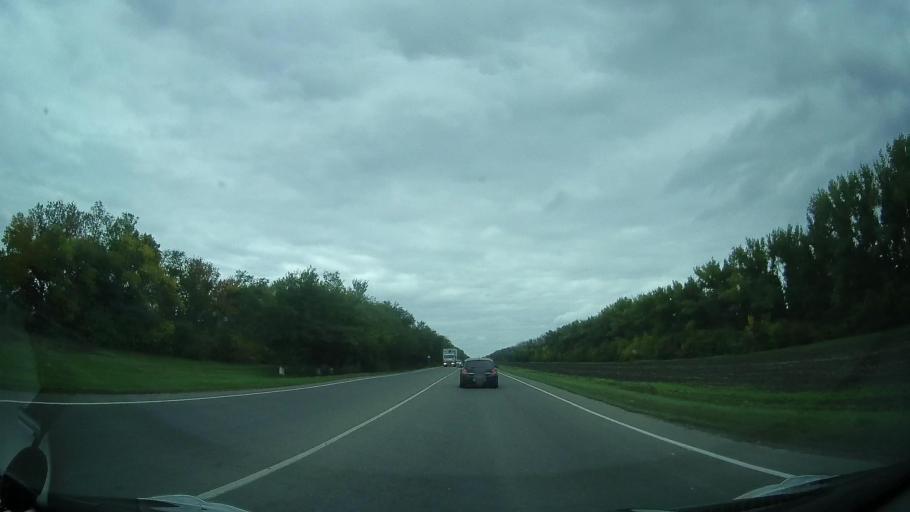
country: RU
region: Rostov
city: Yegorlykskaya
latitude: 46.6011
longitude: 40.6177
